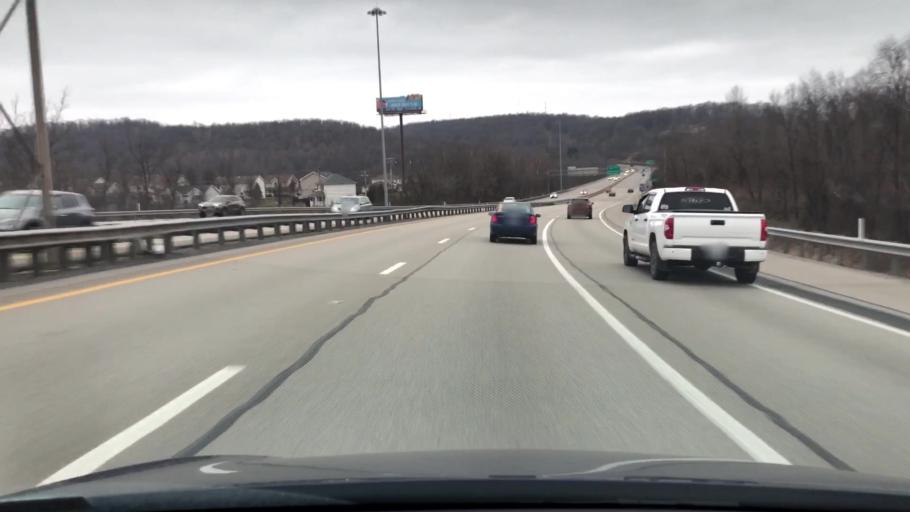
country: US
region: West Virginia
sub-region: Monongalia County
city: Morgantown
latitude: 39.5829
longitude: -79.9790
